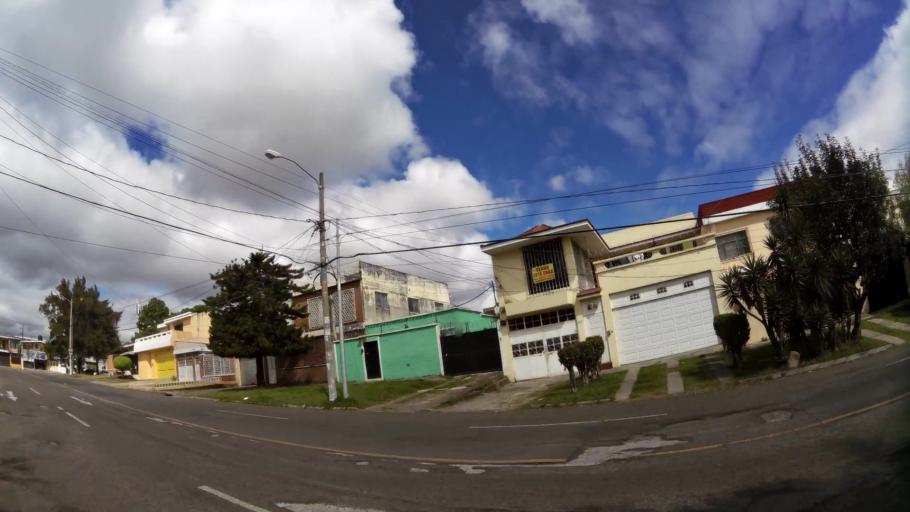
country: GT
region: Guatemala
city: Guatemala City
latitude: 14.6373
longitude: -90.5556
